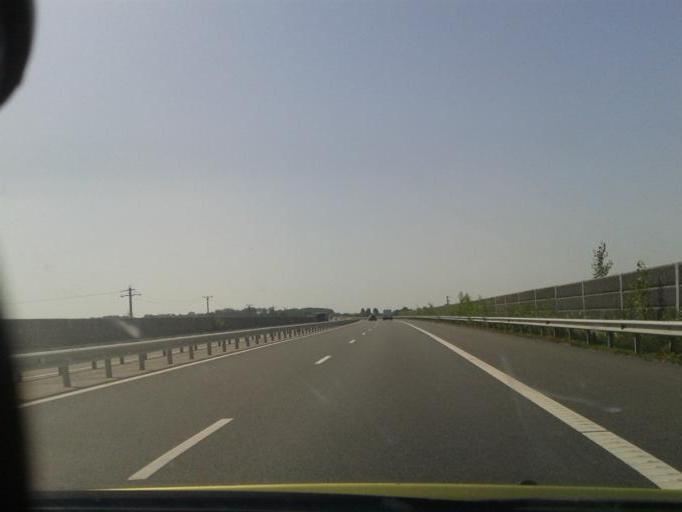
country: RO
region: Prahova
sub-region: Comuna Rafov
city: Rafov
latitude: 44.8735
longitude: 26.1388
